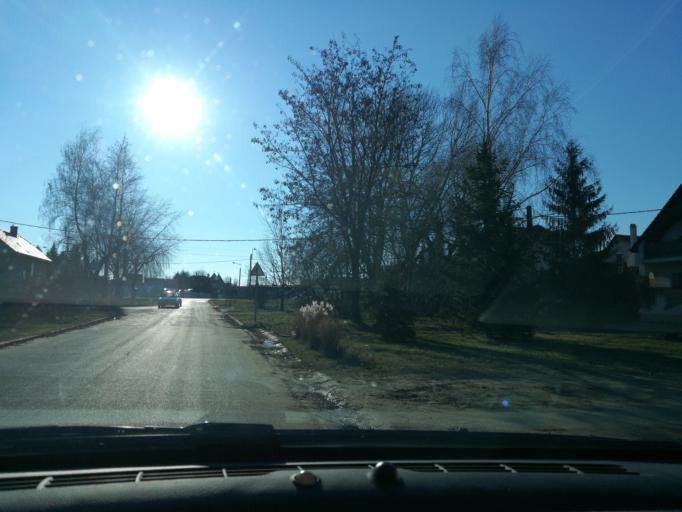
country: HU
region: Szabolcs-Szatmar-Bereg
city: Nyiregyhaza
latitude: 47.9386
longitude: 21.7501
